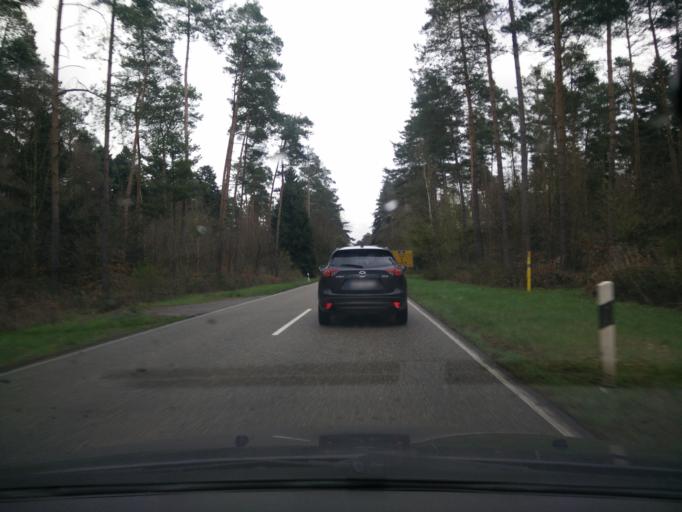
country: DE
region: Rheinland-Pfalz
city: Minfeld
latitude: 49.0504
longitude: 8.1615
